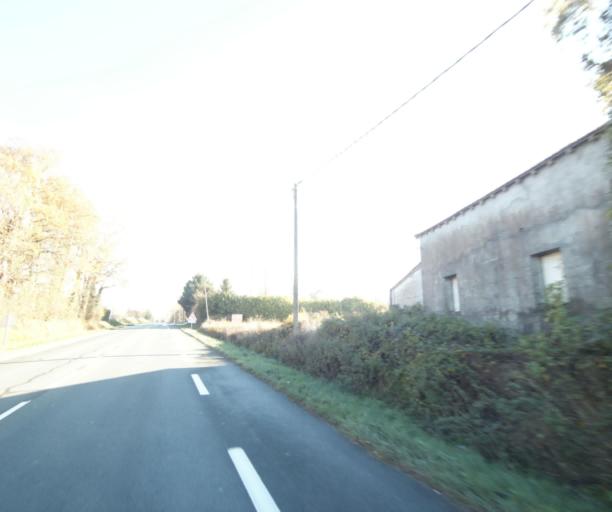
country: FR
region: Poitou-Charentes
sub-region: Departement de la Charente-Maritime
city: Fontcouverte
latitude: 45.7452
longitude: -0.5749
